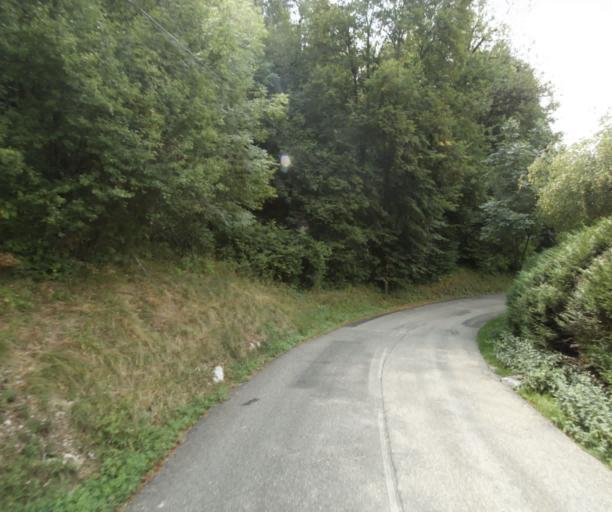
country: FR
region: Rhone-Alpes
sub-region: Departement de l'Isere
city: Le Sappey-en-Chartreuse
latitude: 45.2585
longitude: 5.7471
